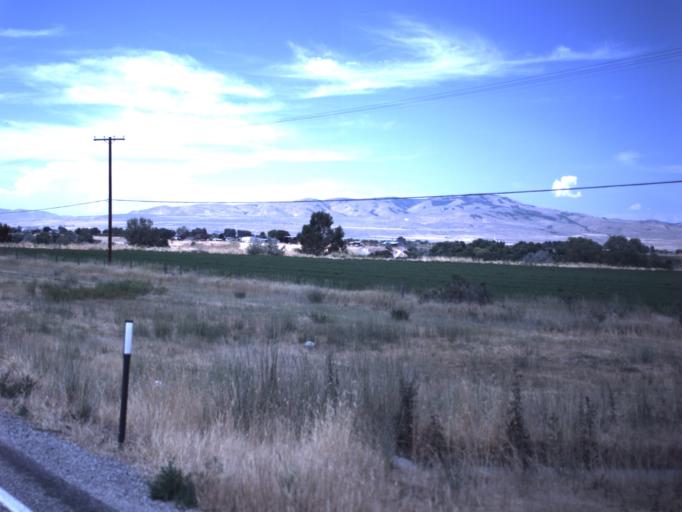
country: US
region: Utah
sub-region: Box Elder County
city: Elwood
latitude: 41.7151
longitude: -112.1051
